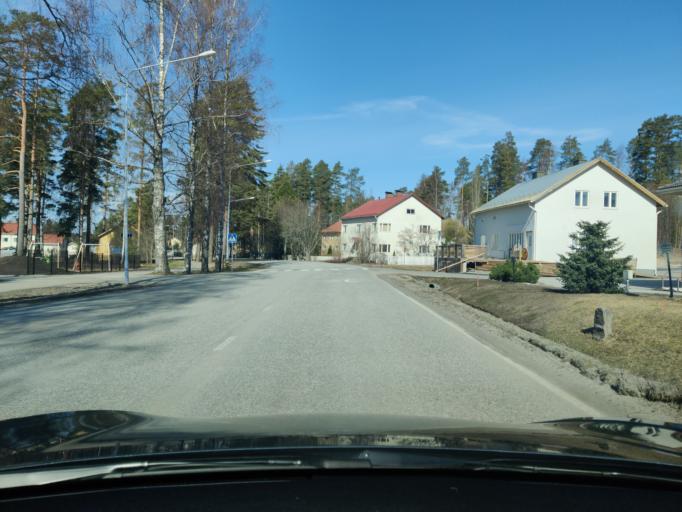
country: FI
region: Northern Savo
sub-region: Kuopio
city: Vehmersalmi
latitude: 62.7617
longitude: 28.0279
